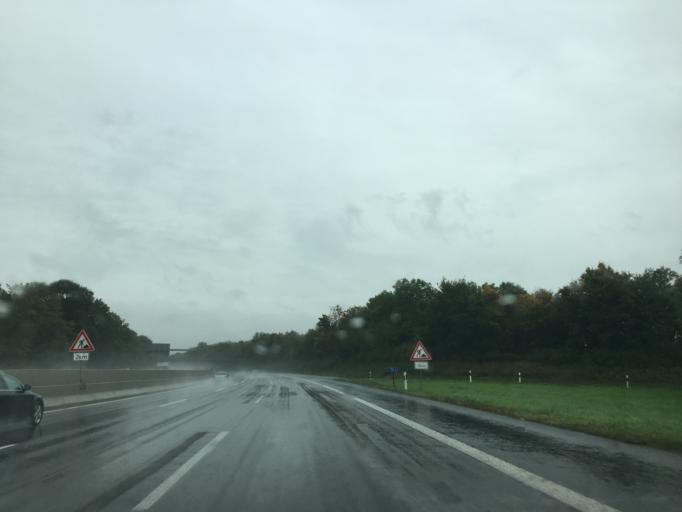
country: DE
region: North Rhine-Westphalia
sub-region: Regierungsbezirk Dusseldorf
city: Dusseldorf
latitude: 51.1641
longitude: 6.7696
